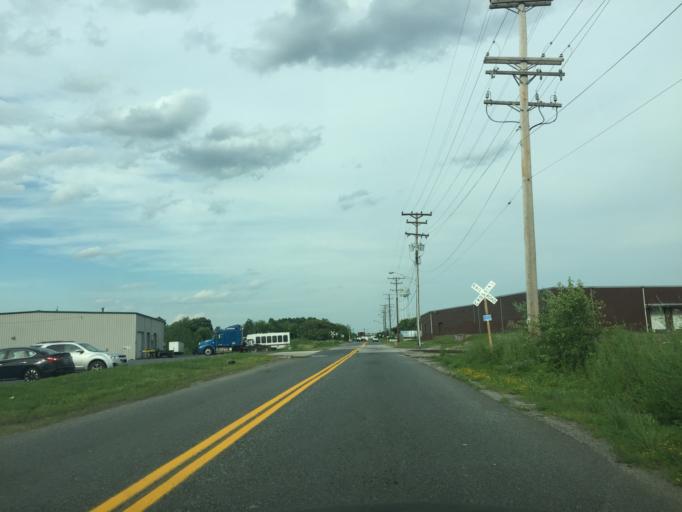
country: US
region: Maryland
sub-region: Baltimore County
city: Rosedale
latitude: 39.3001
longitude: -76.5193
